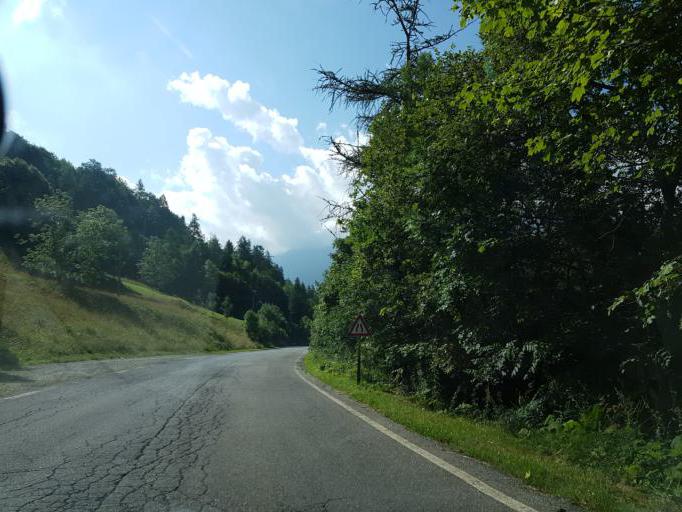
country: IT
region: Piedmont
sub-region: Provincia di Cuneo
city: Casteldelfino
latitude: 44.6068
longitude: 7.0612
